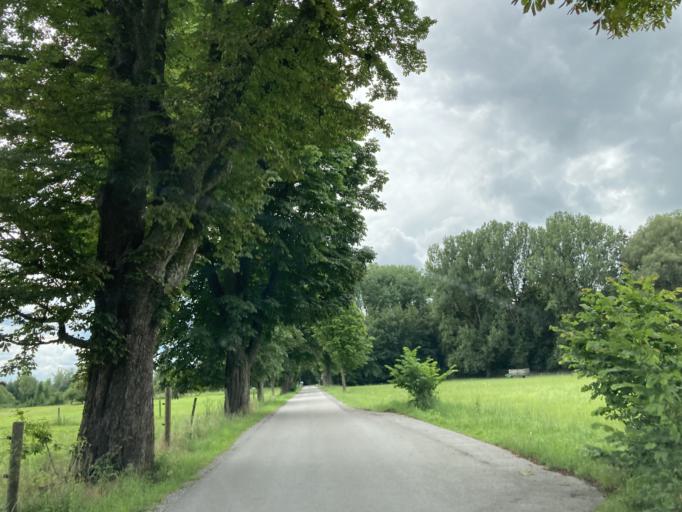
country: DE
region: Bavaria
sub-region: Upper Bavaria
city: Rosenheim
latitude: 47.8673
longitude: 12.1414
